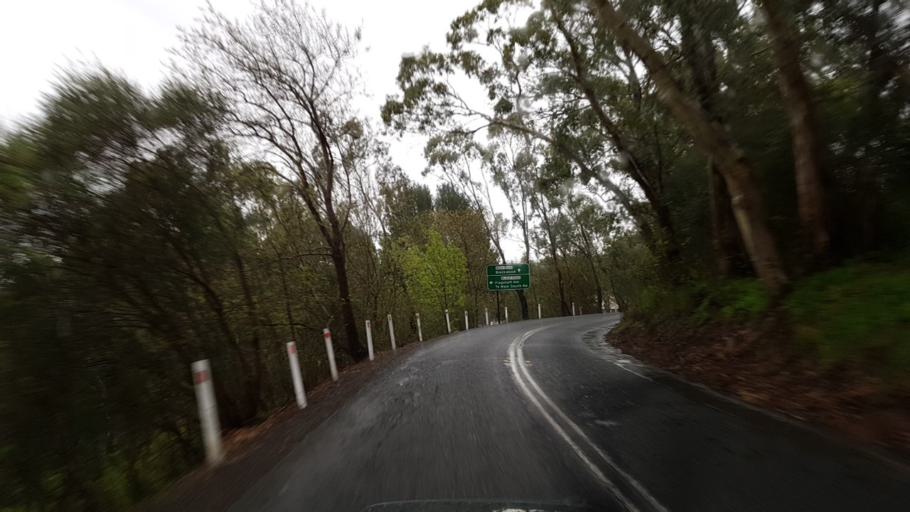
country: AU
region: South Australia
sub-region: Onkaparinga
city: Craigburn Farm
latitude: -35.0610
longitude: 138.6197
